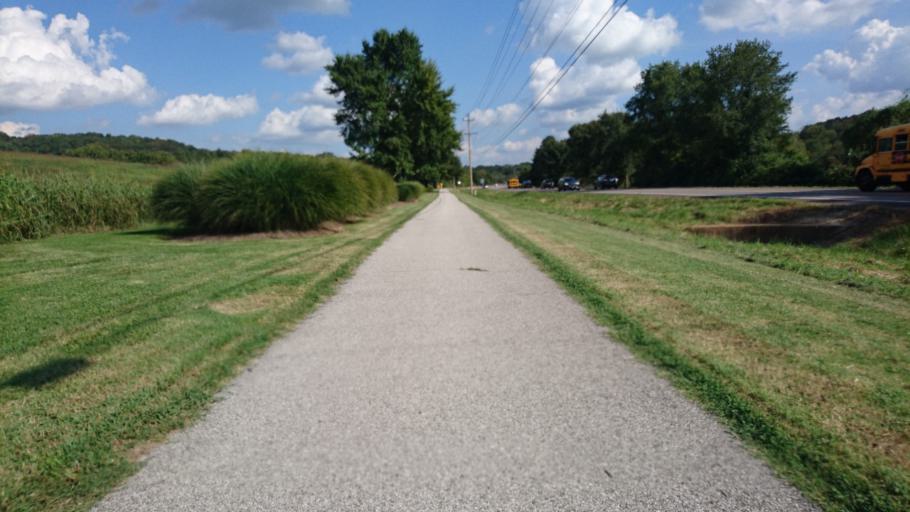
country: US
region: Missouri
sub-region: Saint Louis County
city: Wildwood
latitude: 38.5494
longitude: -90.6349
